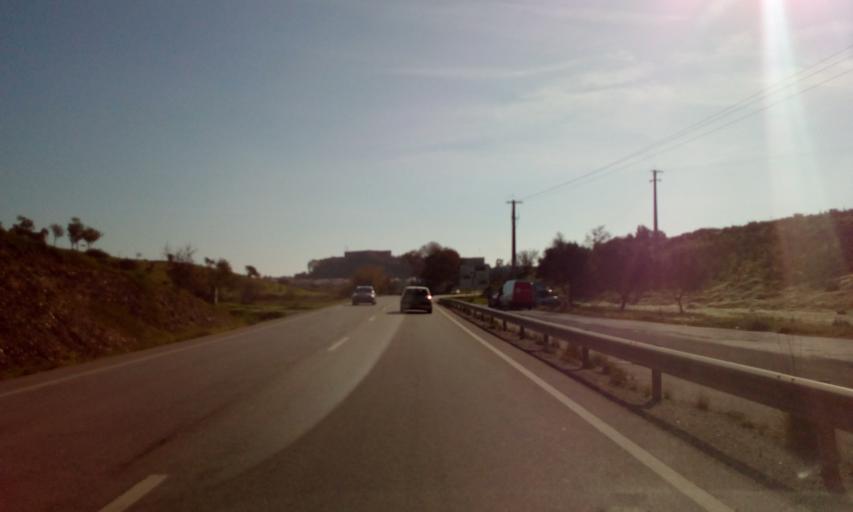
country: PT
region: Faro
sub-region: Castro Marim
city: Castro Marim
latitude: 37.2249
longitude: -7.4458
